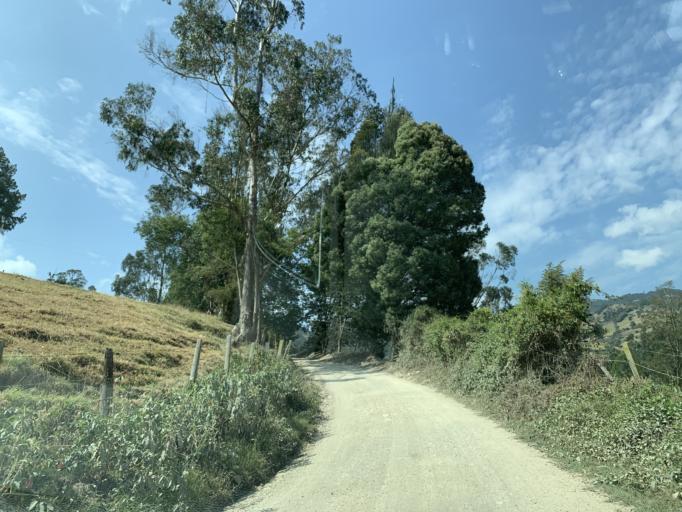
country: CO
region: Boyaca
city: Turmeque
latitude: 5.2806
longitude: -73.5049
